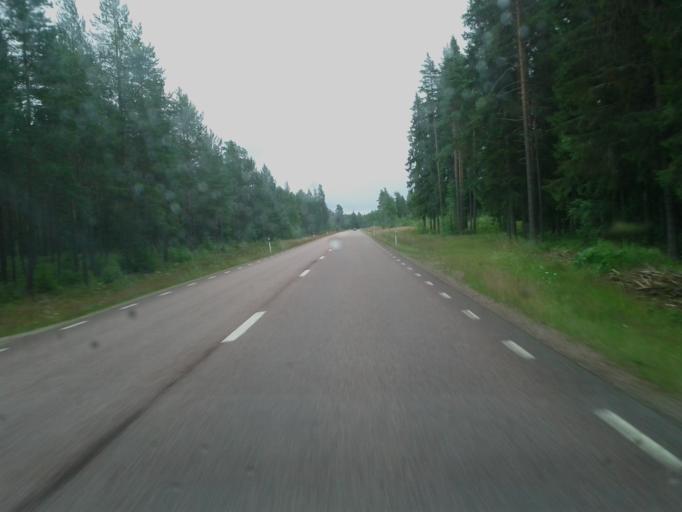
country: SE
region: Dalarna
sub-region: Mora Kommun
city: Mora
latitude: 60.9898
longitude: 14.6734
